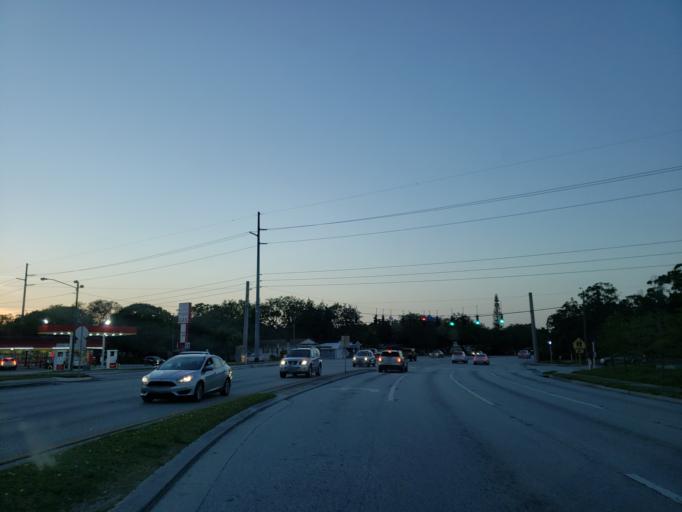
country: US
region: Florida
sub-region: Pinellas County
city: Largo
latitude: 27.9088
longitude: -82.7961
